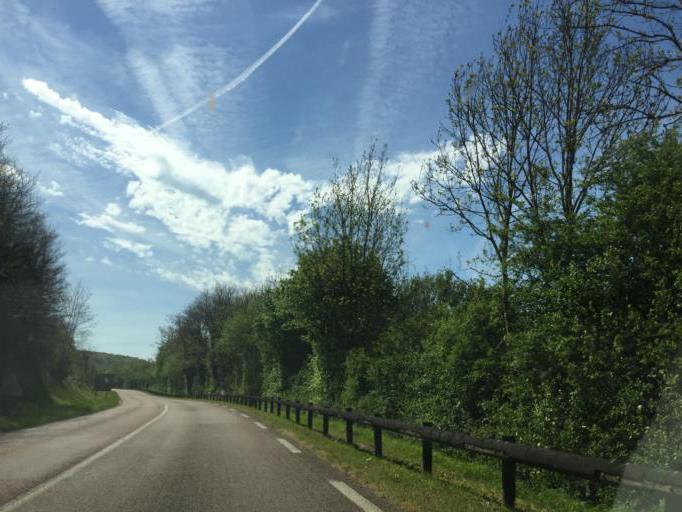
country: FR
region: Bourgogne
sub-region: Departement de la Nievre
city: Clamecy
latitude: 47.4517
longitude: 3.5513
